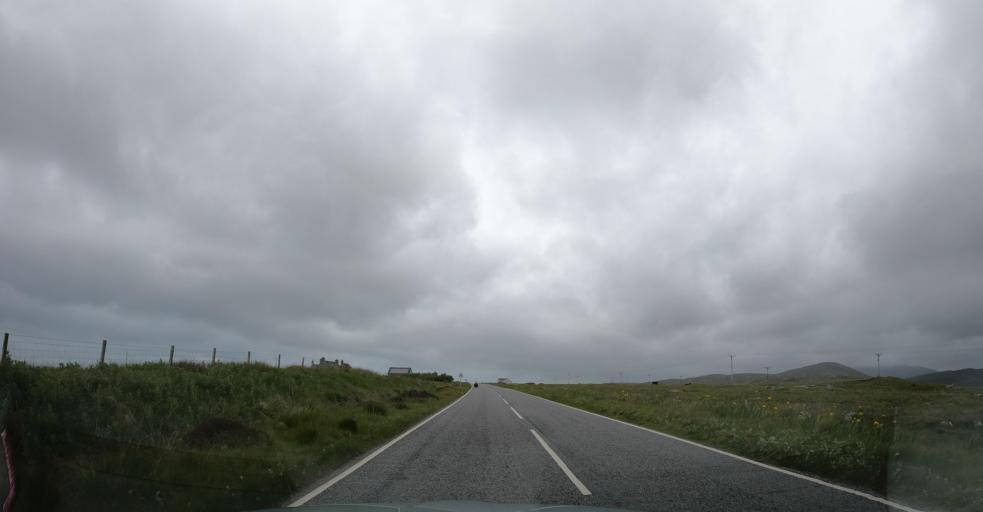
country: GB
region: Scotland
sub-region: Eilean Siar
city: Isle of South Uist
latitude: 57.1959
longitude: -7.3896
